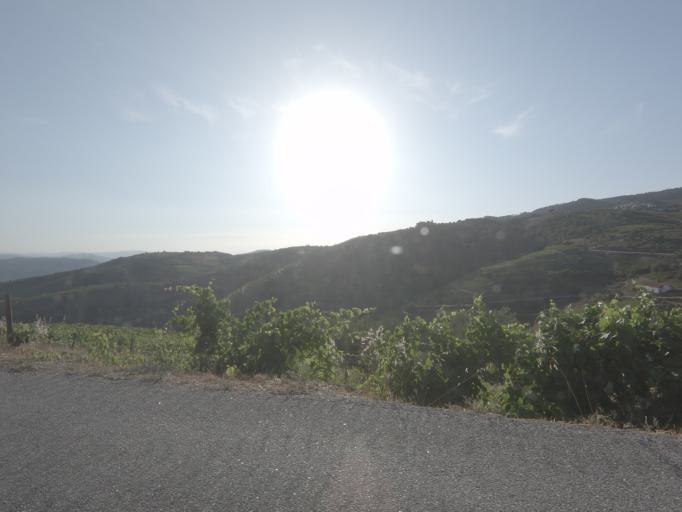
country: PT
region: Vila Real
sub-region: Sabrosa
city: Vilela
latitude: 41.1752
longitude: -7.5982
